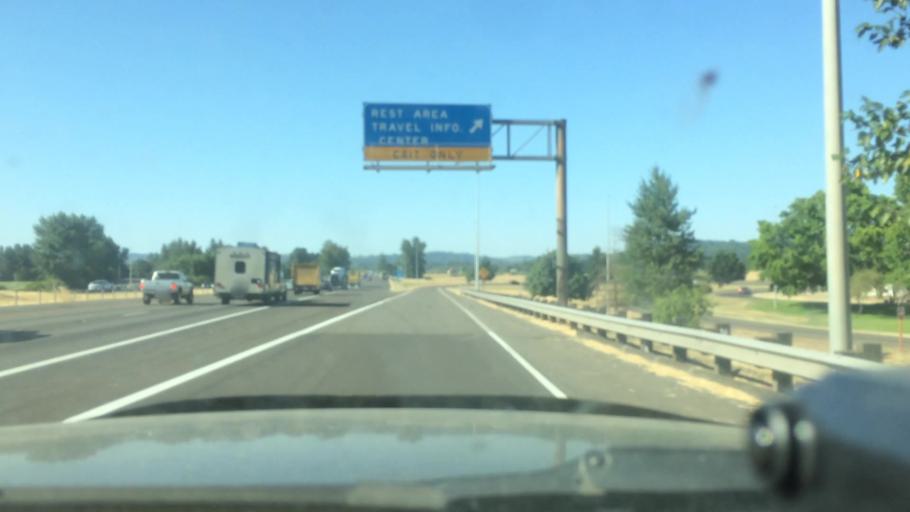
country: US
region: Oregon
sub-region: Marion County
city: Jefferson
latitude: 44.7387
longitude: -123.0524
